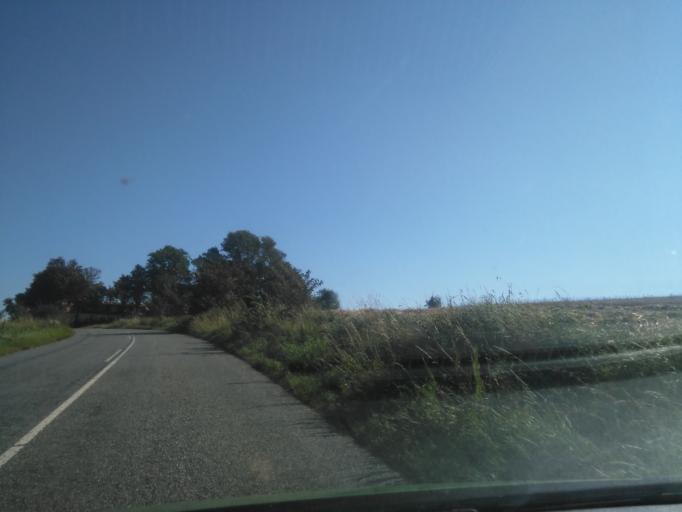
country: DK
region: Central Jutland
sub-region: Syddjurs Kommune
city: Ronde
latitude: 56.1927
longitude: 10.5035
